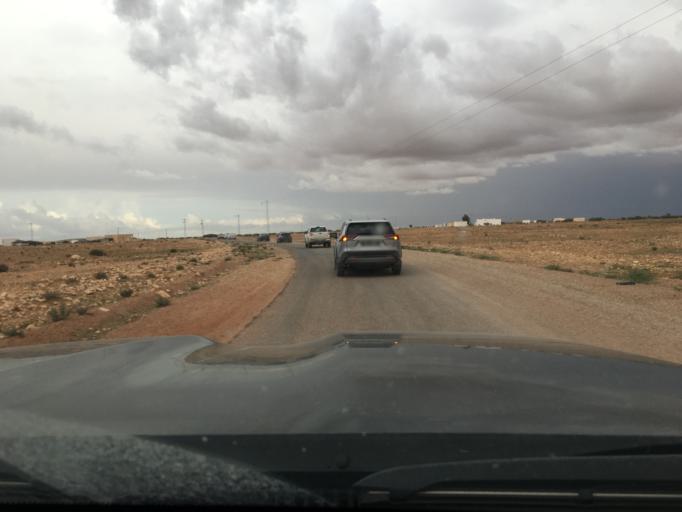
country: TN
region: Madanin
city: Medenine
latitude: 33.2900
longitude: 10.6058
